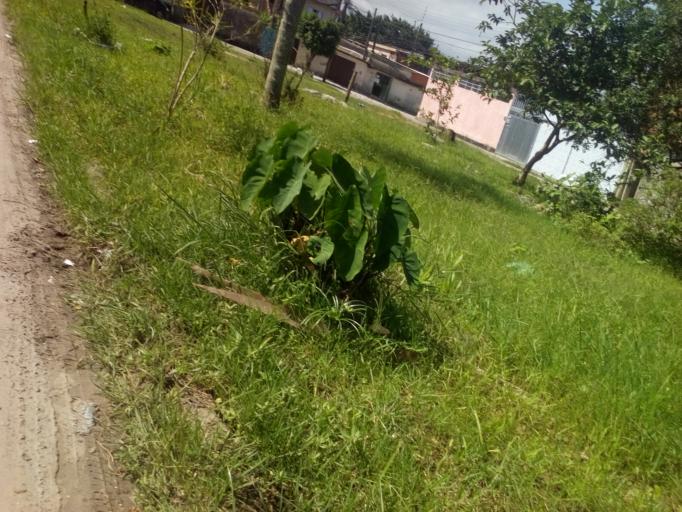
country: BR
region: Sao Paulo
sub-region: Guaruja
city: Guaruja
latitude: -23.9647
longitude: -46.2603
